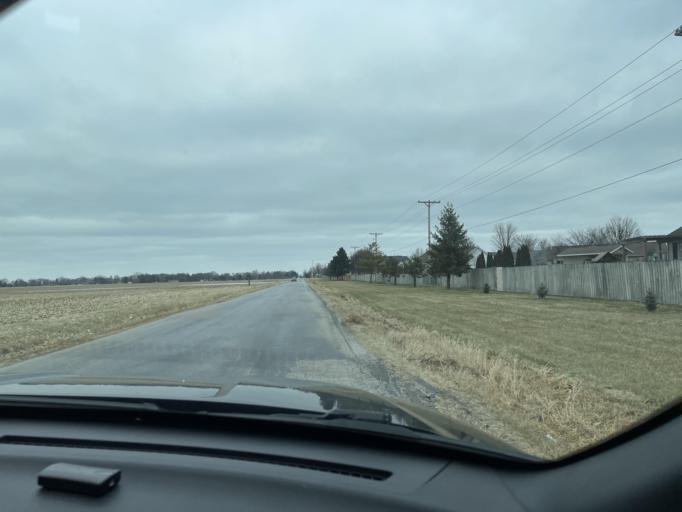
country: US
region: Illinois
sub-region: Sangamon County
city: Jerome
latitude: 39.7737
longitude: -89.7534
